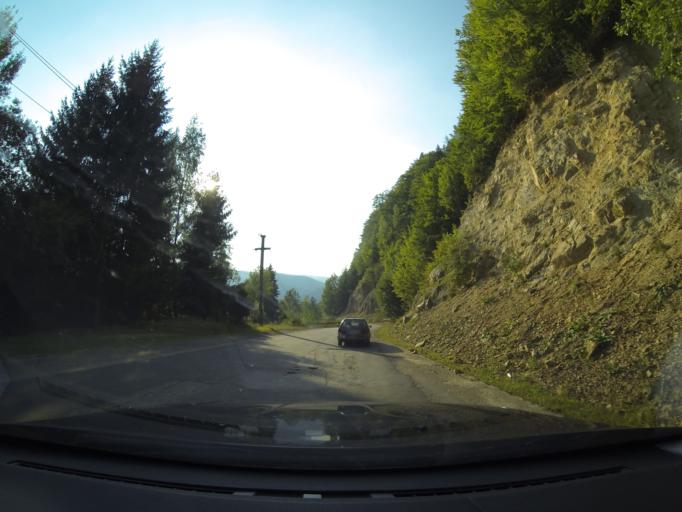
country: RO
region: Arges
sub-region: Comuna Arefu
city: Arefu
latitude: 45.4096
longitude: 24.6326
